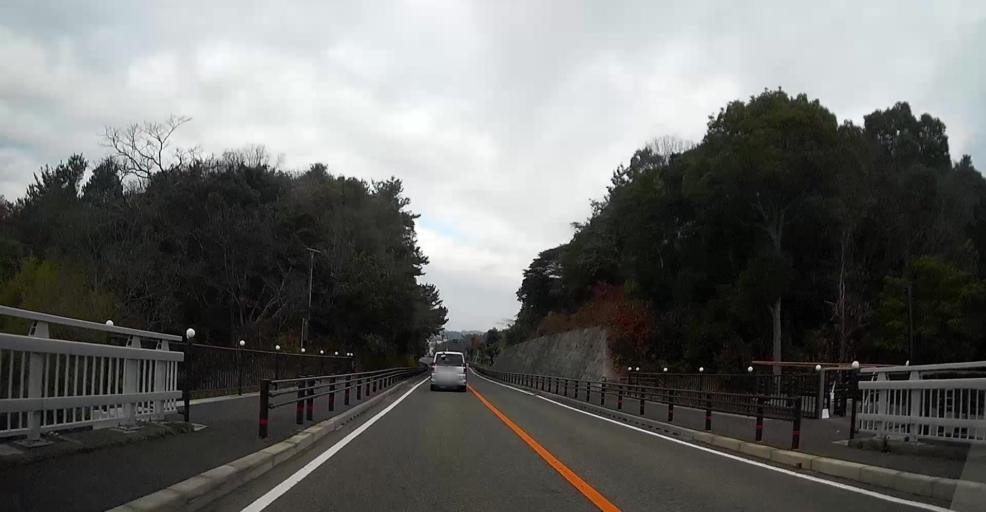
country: JP
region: Kumamoto
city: Yatsushiro
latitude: 32.5396
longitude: 130.4235
